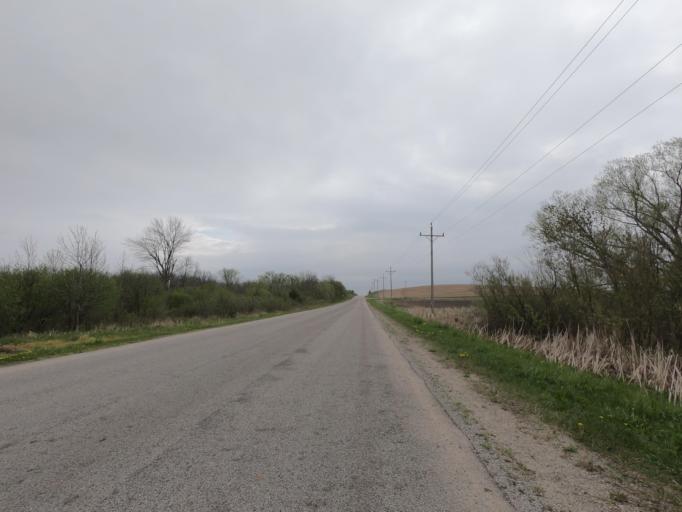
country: US
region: Wisconsin
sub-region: Jefferson County
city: Jefferson
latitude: 43.0319
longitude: -88.7912
